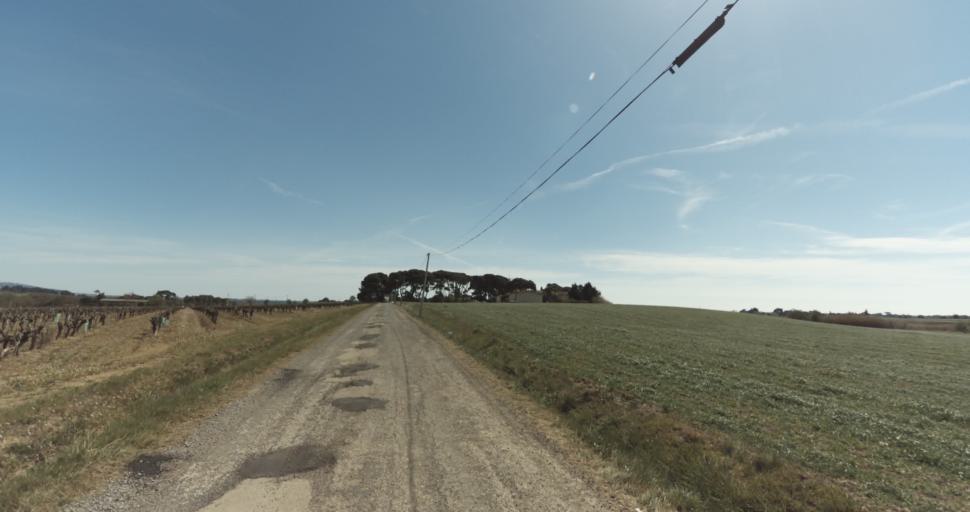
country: FR
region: Languedoc-Roussillon
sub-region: Departement de l'Herault
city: Pinet
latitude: 43.3981
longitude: 3.5406
